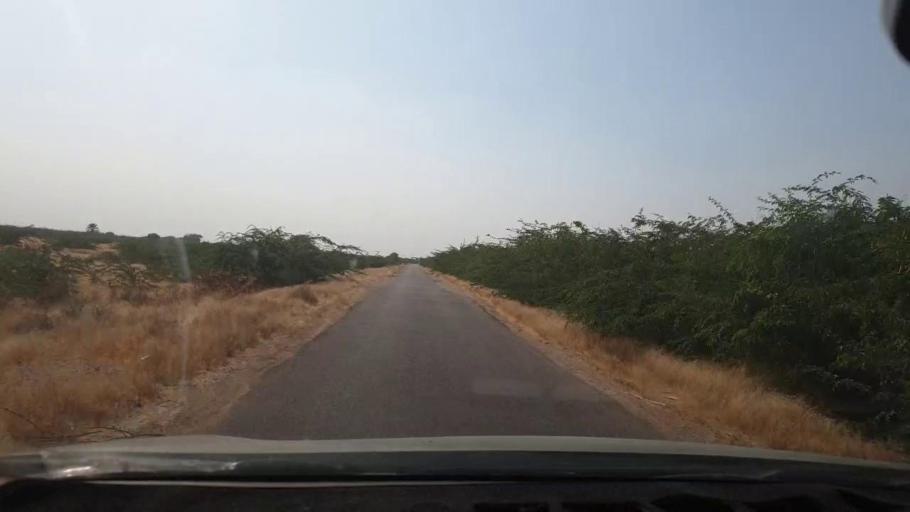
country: PK
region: Sindh
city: Malir Cantonment
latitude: 25.1043
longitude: 67.1981
